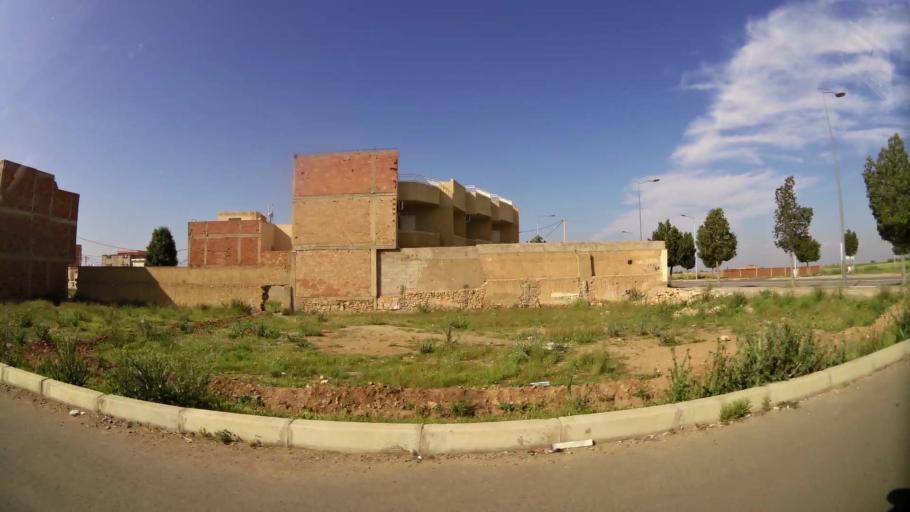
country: MA
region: Oriental
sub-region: Oujda-Angad
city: Oujda
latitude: 34.7178
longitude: -1.8830
